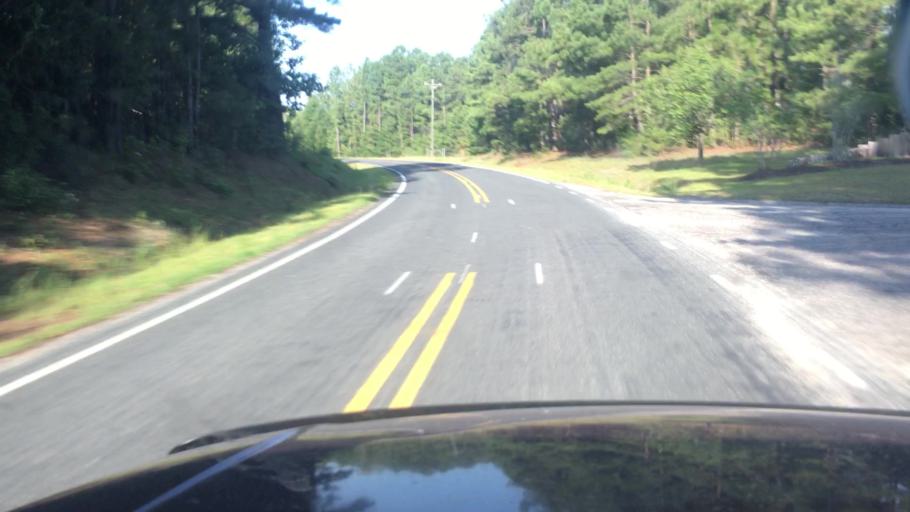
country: US
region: North Carolina
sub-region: Robeson County
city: Saint Pauls
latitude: 34.8548
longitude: -78.8513
